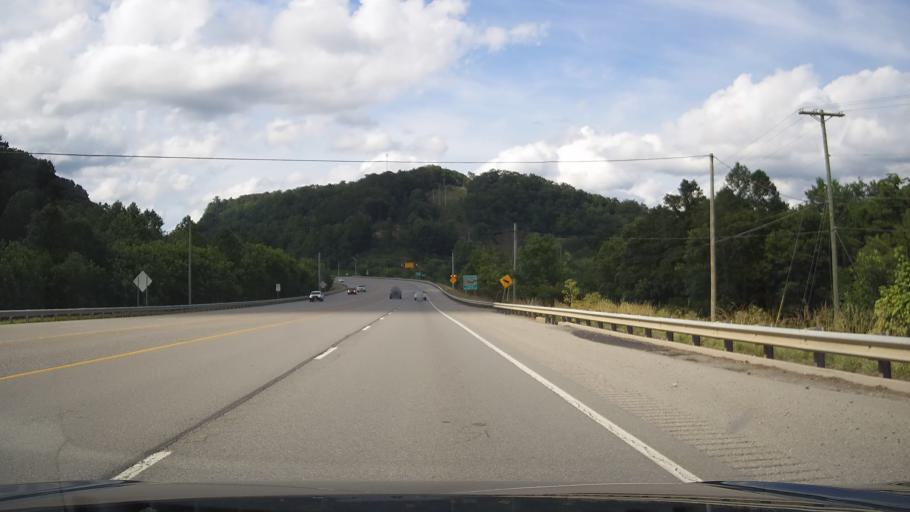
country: US
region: Kentucky
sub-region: Floyd County
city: Prestonsburg
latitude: 37.6823
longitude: -82.7907
